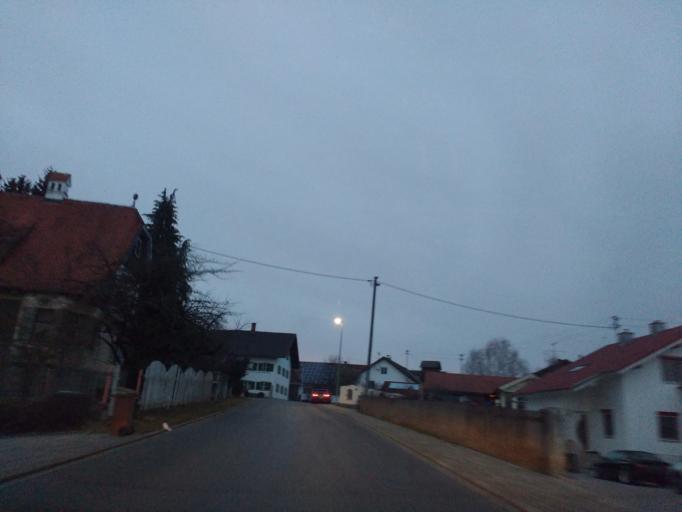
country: DE
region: Bavaria
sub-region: Upper Bavaria
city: Bernbeuren
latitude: 47.7718
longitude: 10.7500
